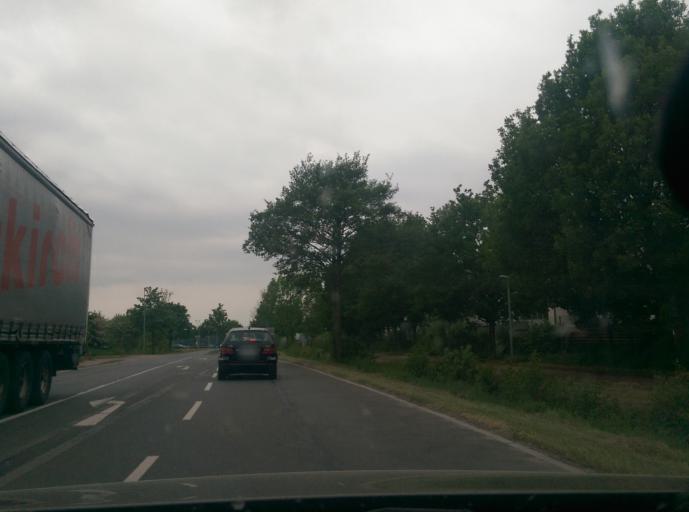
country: DE
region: Lower Saxony
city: Garbsen-Mitte
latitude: 52.4466
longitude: 9.5965
